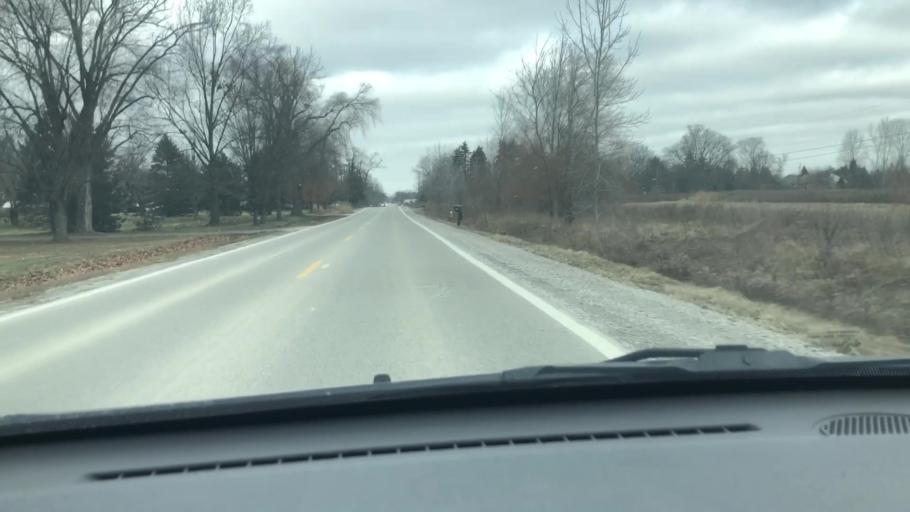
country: US
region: Michigan
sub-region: Macomb County
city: Romeo
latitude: 42.7362
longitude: -83.0172
